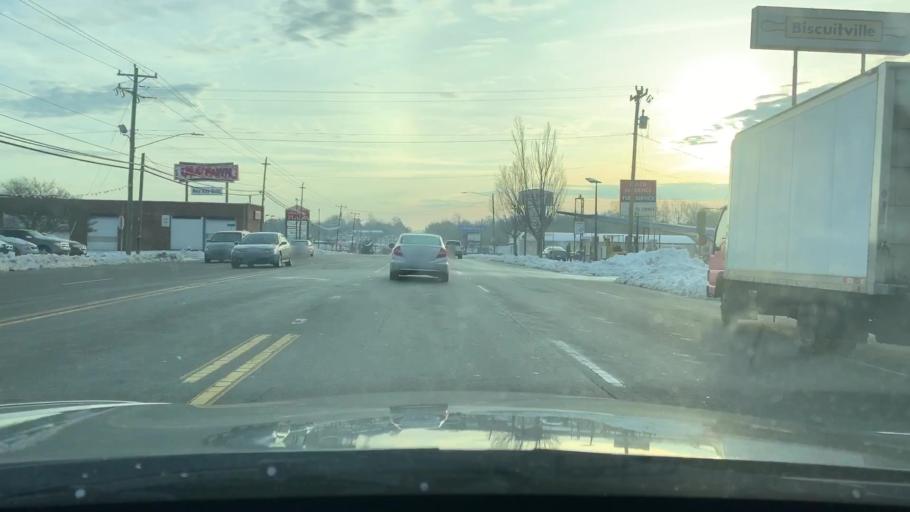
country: US
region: North Carolina
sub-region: Alamance County
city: Graham
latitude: 36.0945
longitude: -79.4025
